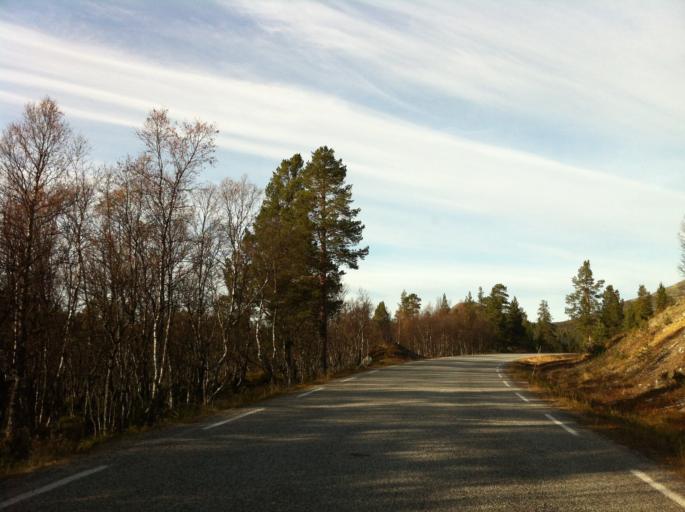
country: NO
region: Hedmark
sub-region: Engerdal
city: Engerdal
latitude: 62.1028
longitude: 12.0261
